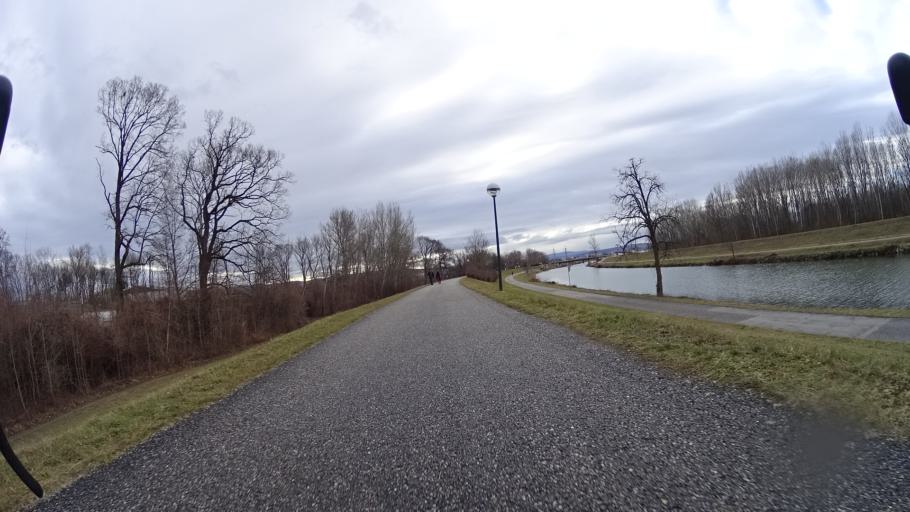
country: AT
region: Lower Austria
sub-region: Politischer Bezirk Tulln
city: Tulln
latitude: 48.3297
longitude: 16.0302
